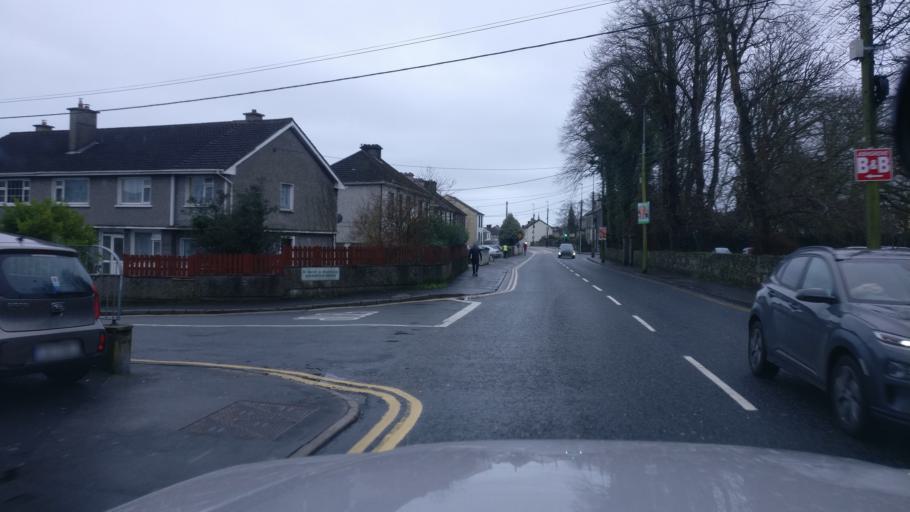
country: IE
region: Connaught
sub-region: County Galway
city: Gaillimh
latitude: 53.2754
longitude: -9.0634
